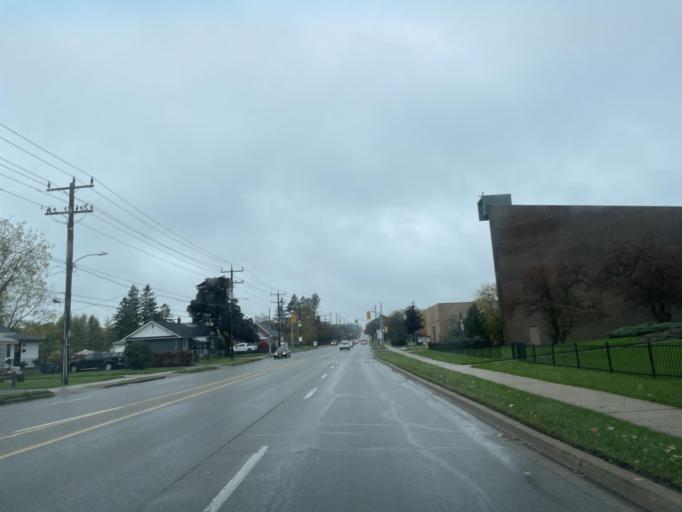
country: CA
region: Ontario
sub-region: Wellington County
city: Guelph
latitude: 43.5586
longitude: -80.2331
